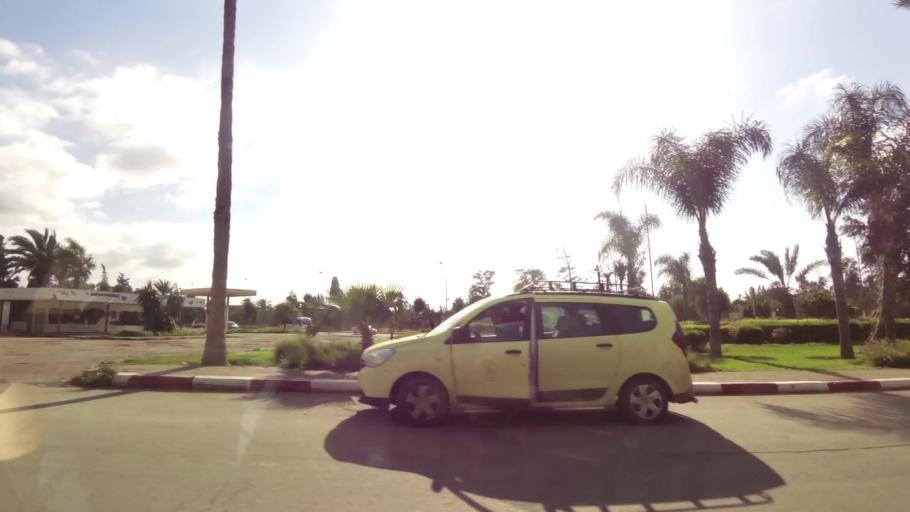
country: MA
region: Chaouia-Ouardigha
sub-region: Settat Province
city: Berrechid
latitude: 33.2603
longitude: -7.5810
